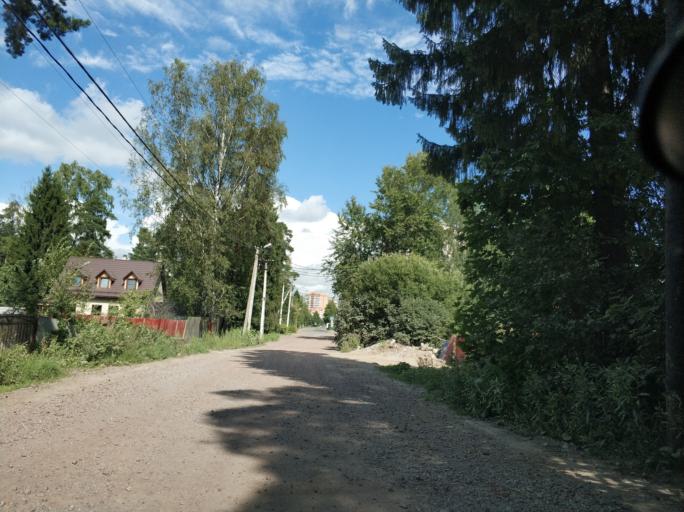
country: RU
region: Leningrad
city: Vsevolozhsk
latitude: 60.0218
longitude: 30.6190
